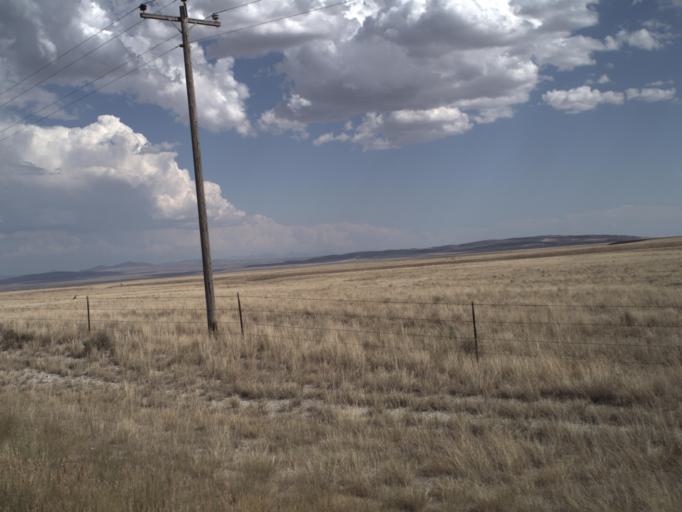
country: US
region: Idaho
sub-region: Minidoka County
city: Rupert
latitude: 41.9703
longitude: -113.1246
